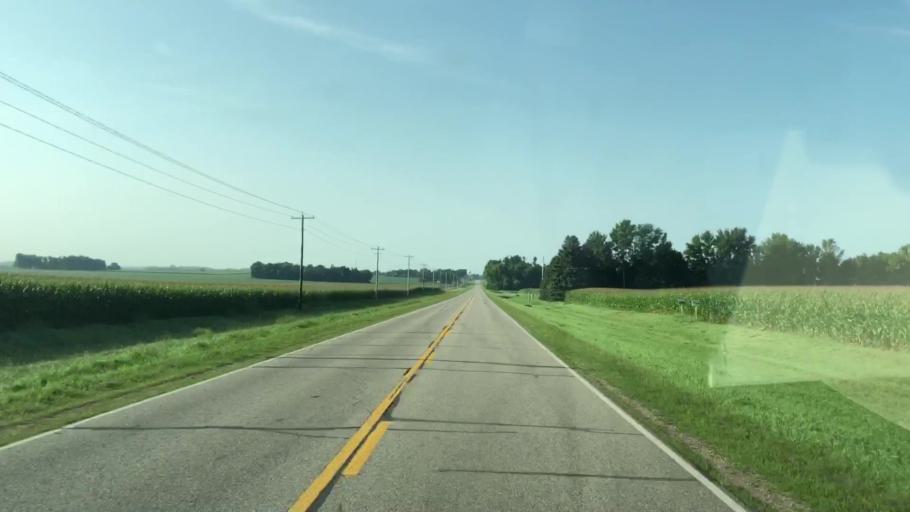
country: US
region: Iowa
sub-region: Lyon County
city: George
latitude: 43.3714
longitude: -95.9982
